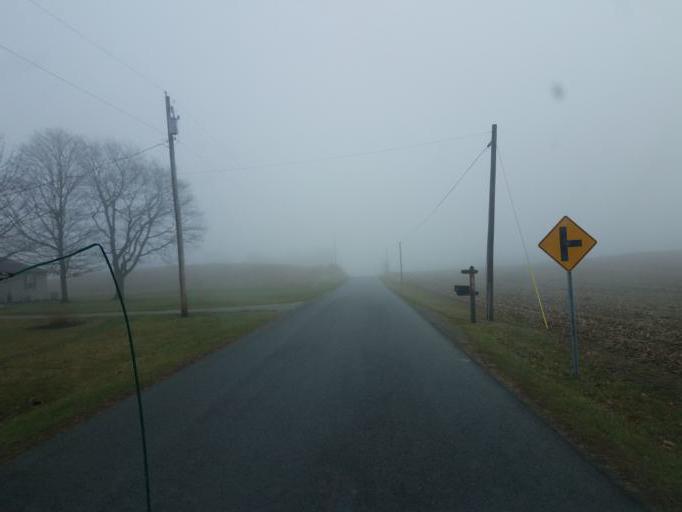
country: US
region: Ohio
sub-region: Champaign County
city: North Lewisburg
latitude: 40.2914
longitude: -83.6310
